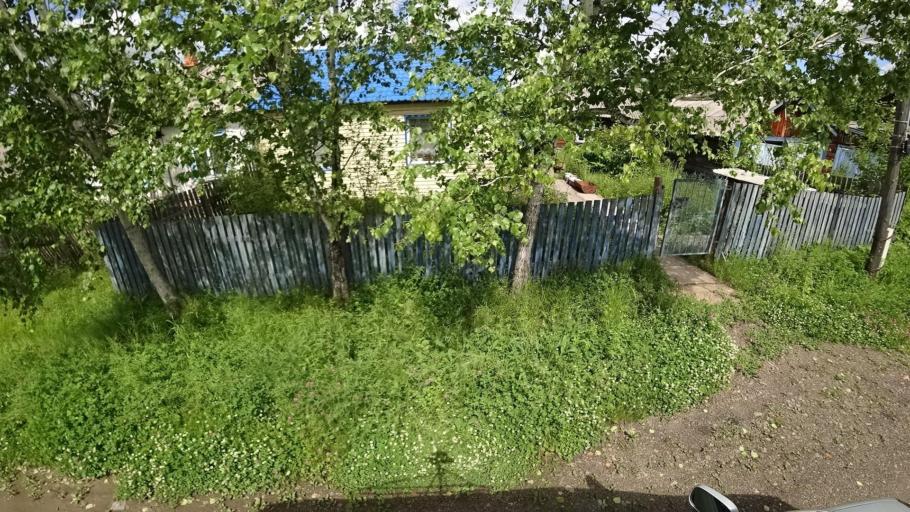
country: RU
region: Khabarovsk Krai
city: Litovko
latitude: 49.3677
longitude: 135.1660
